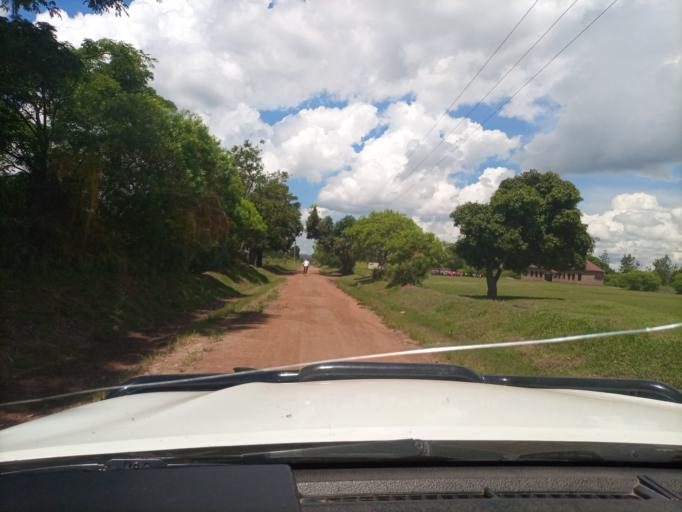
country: UG
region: Eastern Region
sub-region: Tororo District
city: Tororo
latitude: 0.6485
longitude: 33.9966
